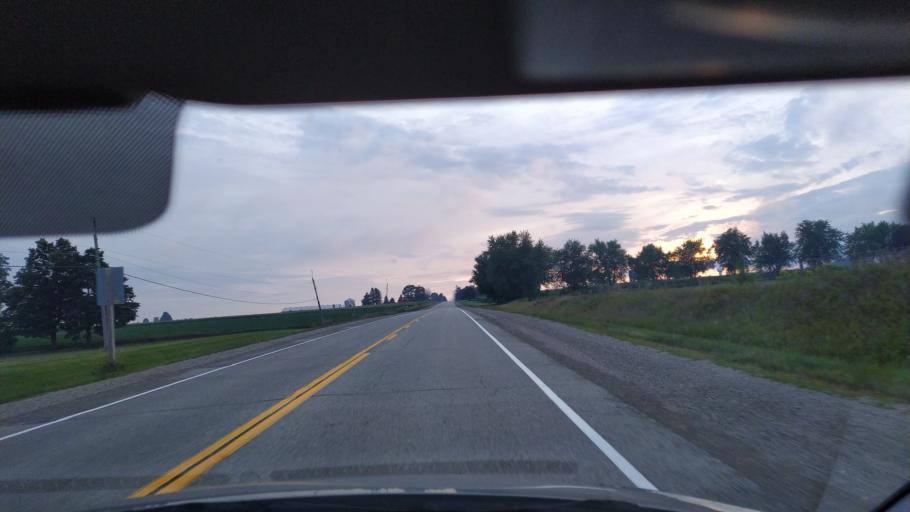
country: CA
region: Ontario
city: Kitchener
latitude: 43.3084
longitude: -80.5889
